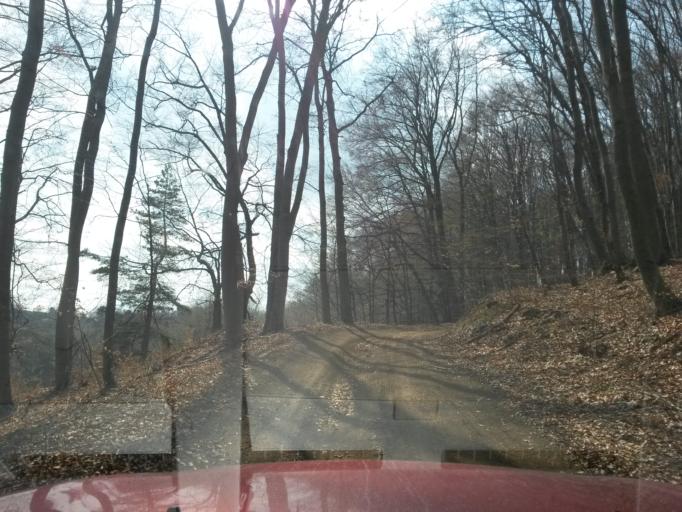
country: SK
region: Presovsky
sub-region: Okres Presov
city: Presov
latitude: 48.9295
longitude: 21.1416
